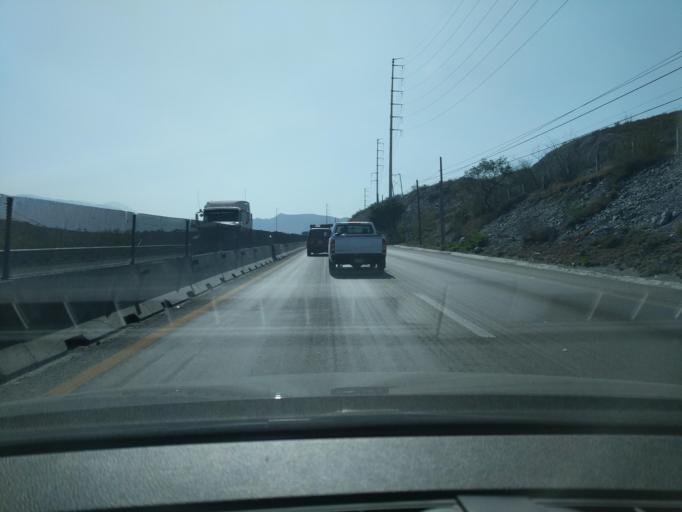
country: MX
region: Nuevo Leon
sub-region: Garcia
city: Los Parques
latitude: 25.7533
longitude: -100.5039
